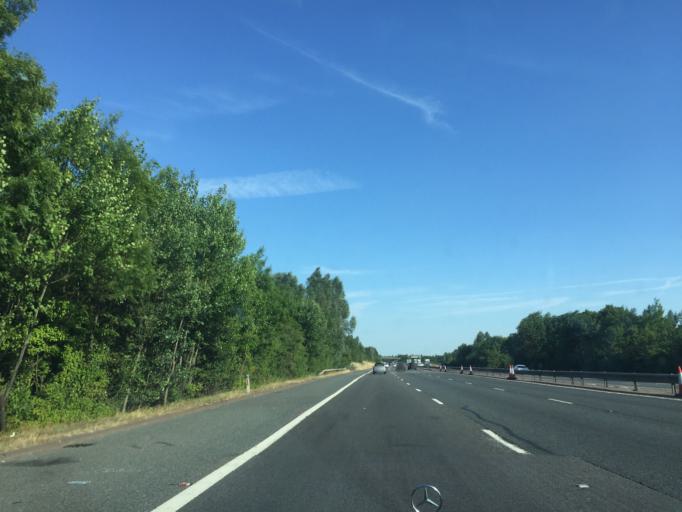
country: GB
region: England
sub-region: Oxfordshire
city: Bicester
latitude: 51.8571
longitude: -1.1805
